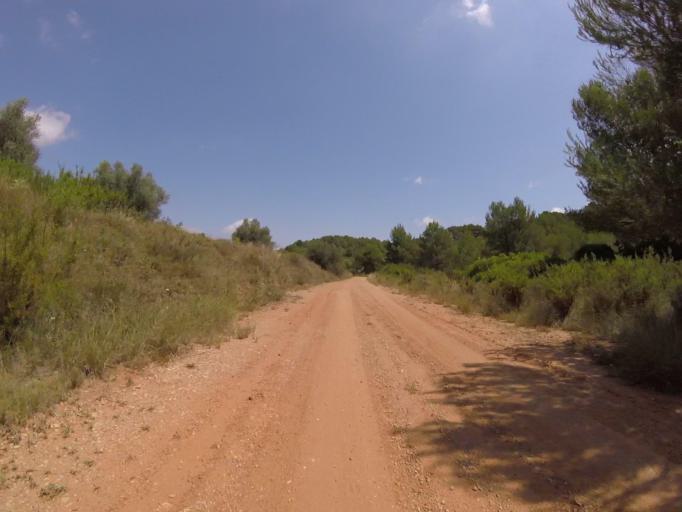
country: ES
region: Valencia
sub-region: Provincia de Castello
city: Torreblanca
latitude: 40.2144
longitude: 0.1470
